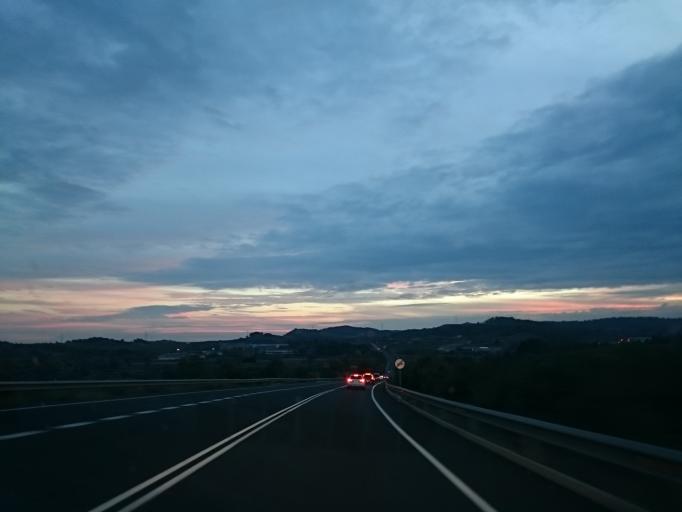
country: ES
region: Catalonia
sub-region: Provincia de Barcelona
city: Sant Pere de Riudebitlles
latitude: 41.4597
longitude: 1.6949
